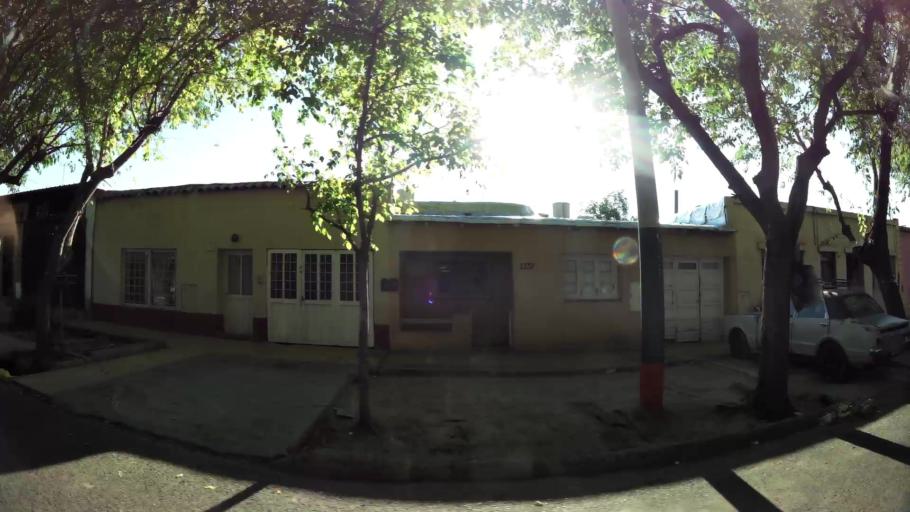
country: AR
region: Mendoza
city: Mendoza
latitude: -32.9083
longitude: -68.8288
